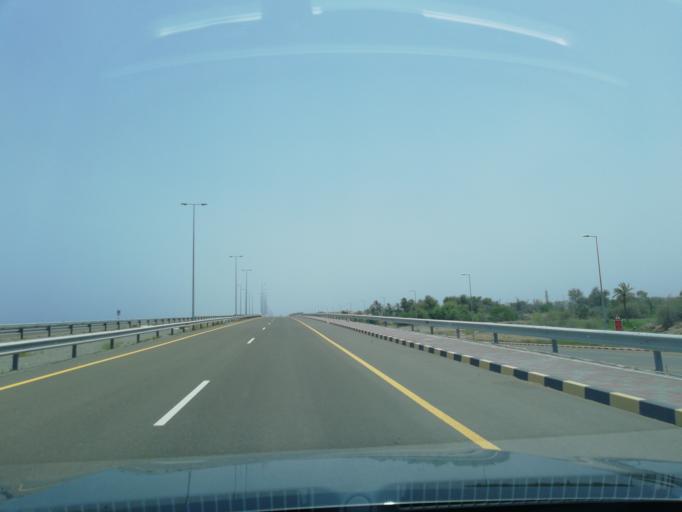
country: OM
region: Al Batinah
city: Shinas
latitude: 24.7696
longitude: 56.4595
